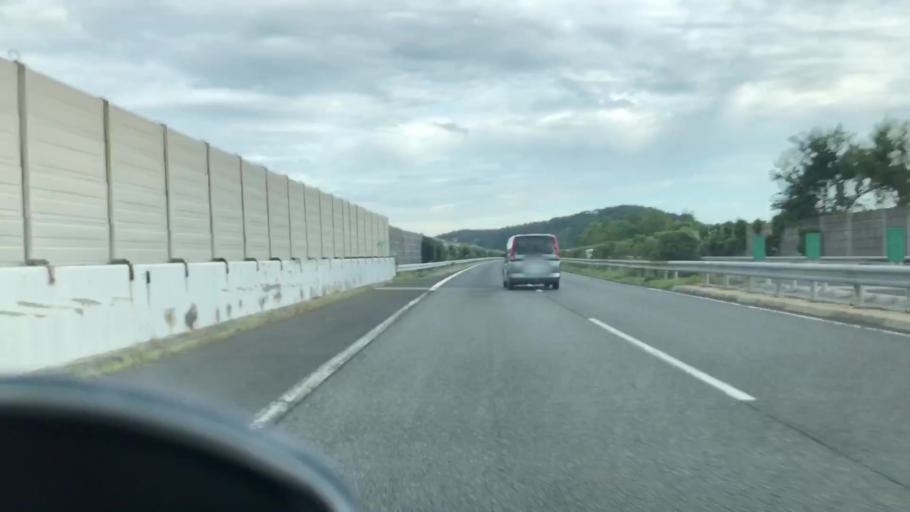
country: JP
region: Hyogo
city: Yashiro
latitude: 34.9057
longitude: 135.0647
